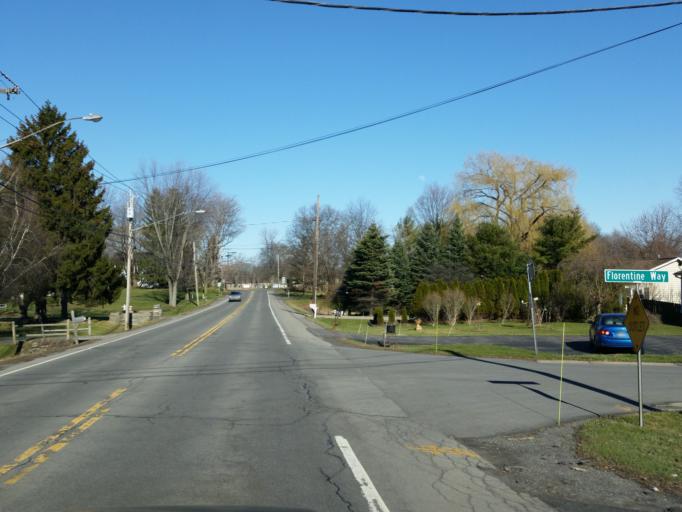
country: US
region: New York
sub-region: Monroe County
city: Scottsville
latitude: 43.0961
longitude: -77.7695
